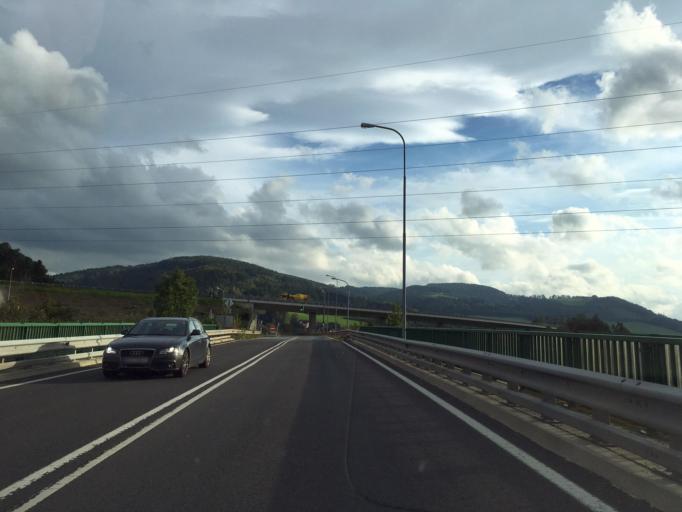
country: AT
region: Lower Austria
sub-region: Politischer Bezirk Neunkirchen
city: Grimmenstein
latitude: 47.6105
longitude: 16.1248
